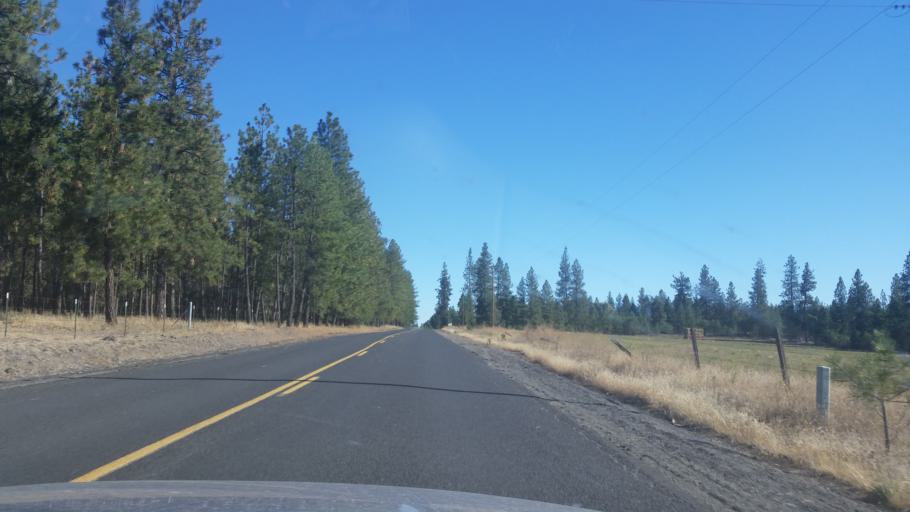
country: US
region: Washington
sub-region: Spokane County
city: Cheney
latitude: 47.5464
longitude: -117.4816
